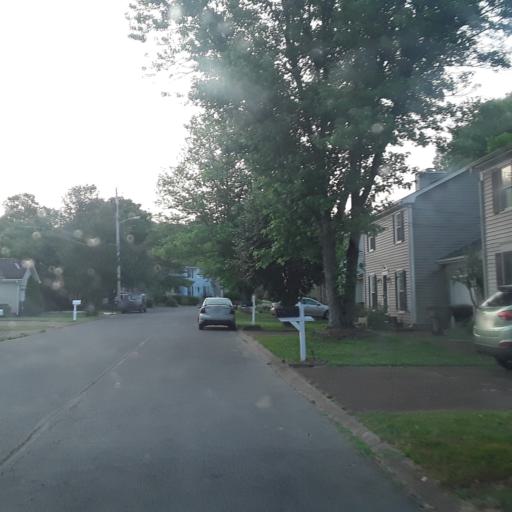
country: US
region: Tennessee
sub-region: Williamson County
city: Brentwood Estates
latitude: 36.0466
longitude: -86.7294
